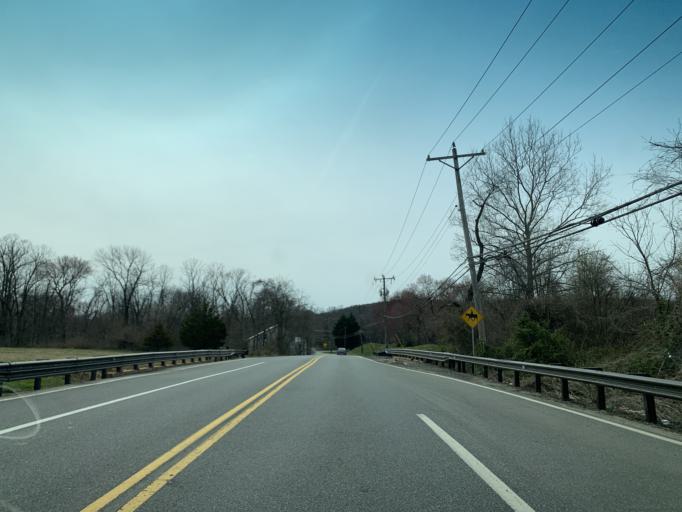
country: US
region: Delaware
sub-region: New Castle County
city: Brookside
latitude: 39.6415
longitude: -75.7326
